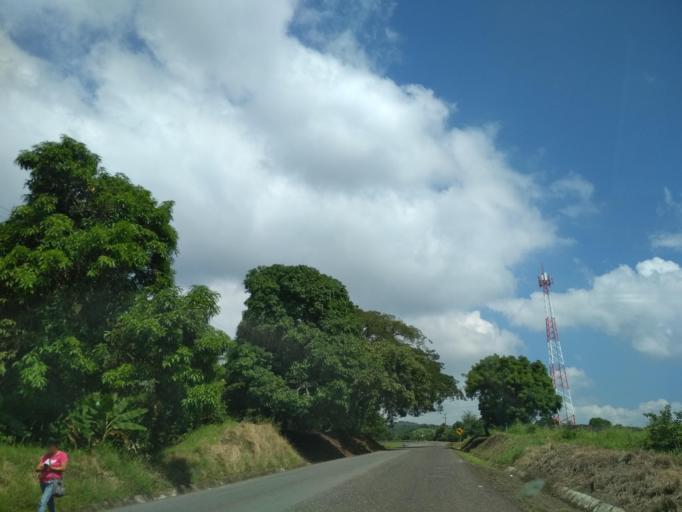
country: MX
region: Veracruz
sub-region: San Andres Tuxtla
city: Texcaltitan Xoteapan (Texcaltitan)
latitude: 18.4384
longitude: -95.2637
